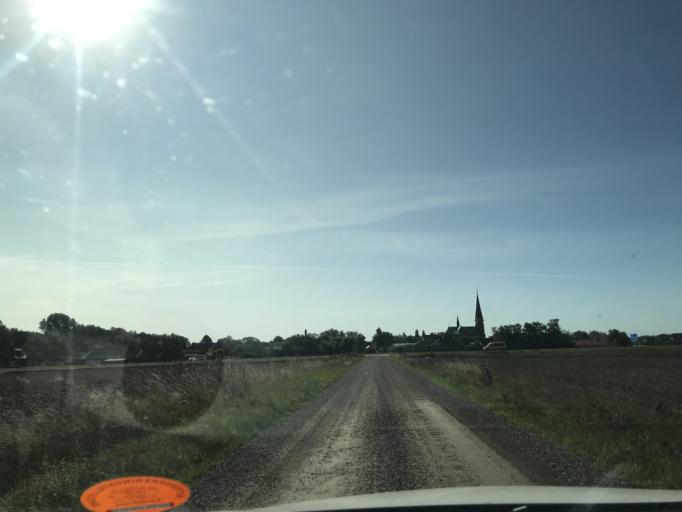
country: SE
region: Skane
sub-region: Landskrona
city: Asmundtorp
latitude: 55.8921
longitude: 12.9487
